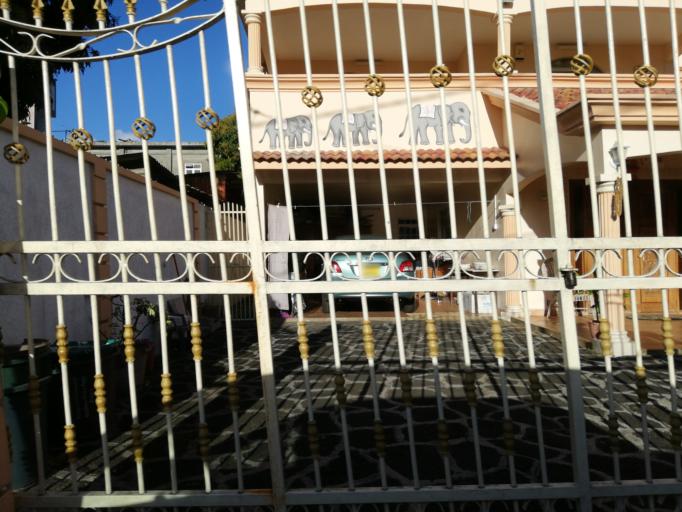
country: MU
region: Moka
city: Moka
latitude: -20.2218
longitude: 57.4706
